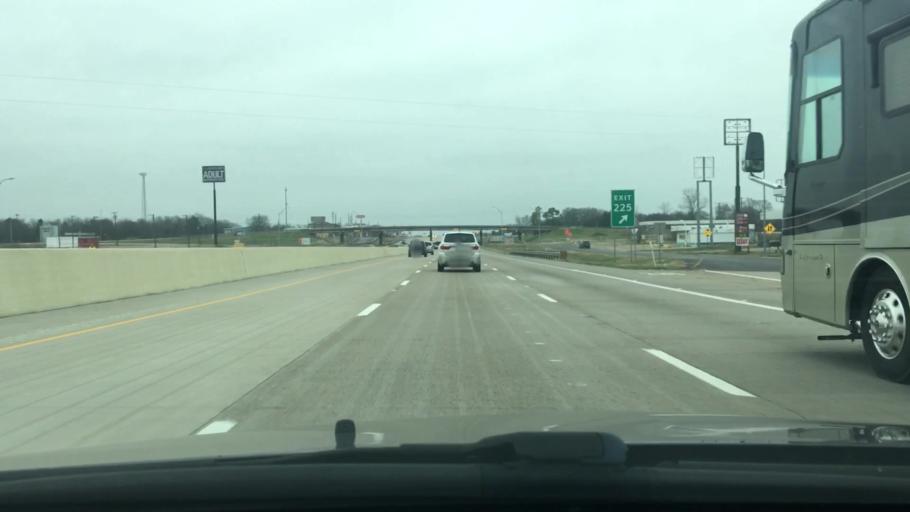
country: US
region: Texas
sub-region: Navarro County
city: Corsicana
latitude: 32.0116
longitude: -96.4354
